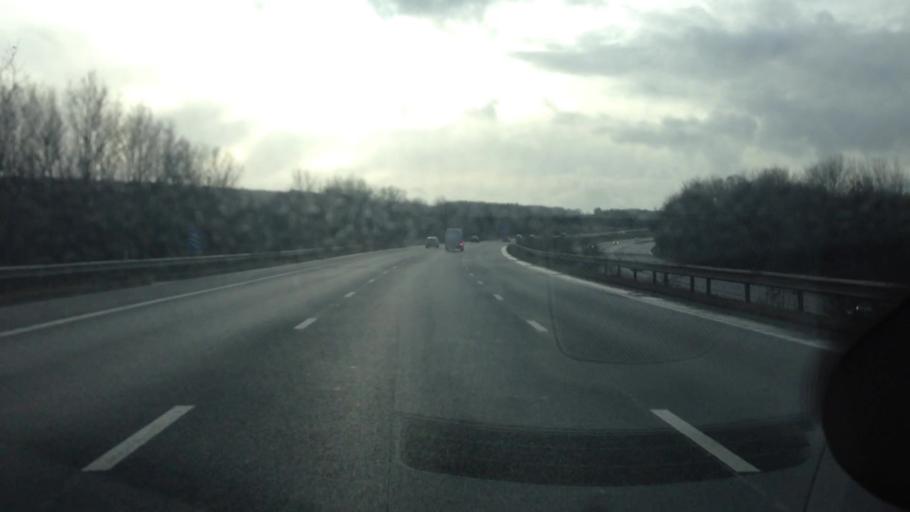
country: GB
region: England
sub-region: City and Borough of Wakefield
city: Crigglestone
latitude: 53.6322
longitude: -1.5397
